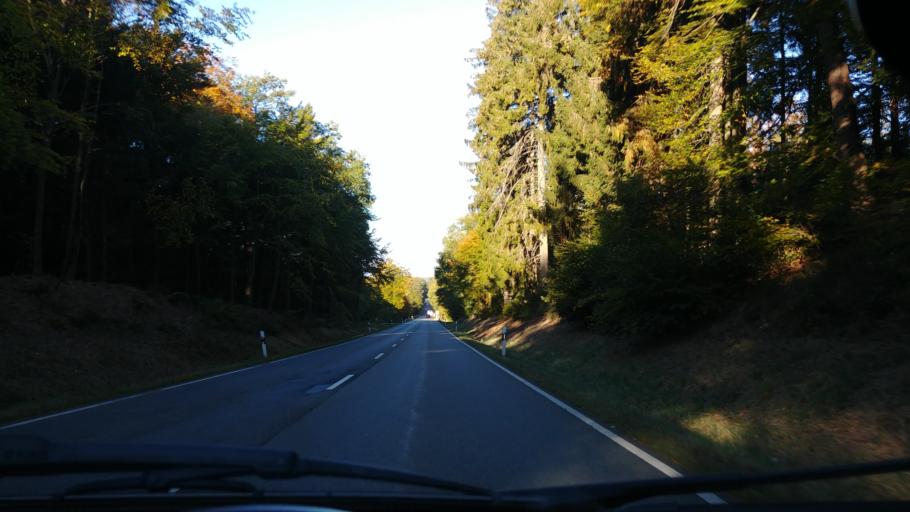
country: DE
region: Rheinland-Pfalz
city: Rettert
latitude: 50.2075
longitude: 7.9373
